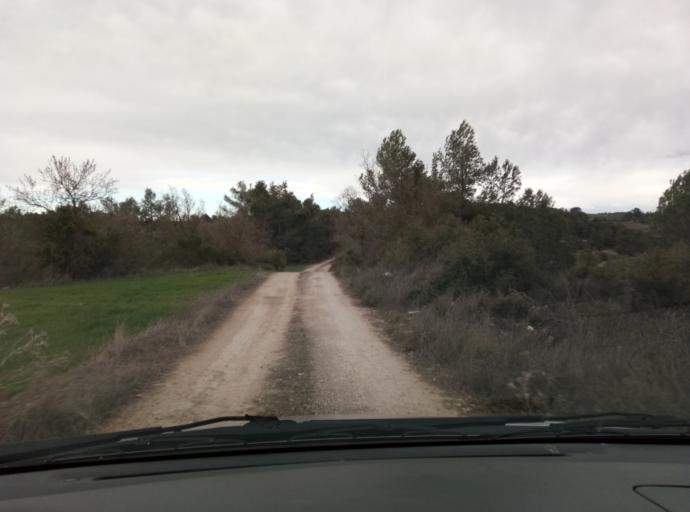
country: ES
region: Catalonia
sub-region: Provincia de Lleida
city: Ciutadilla
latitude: 41.5161
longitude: 1.1477
